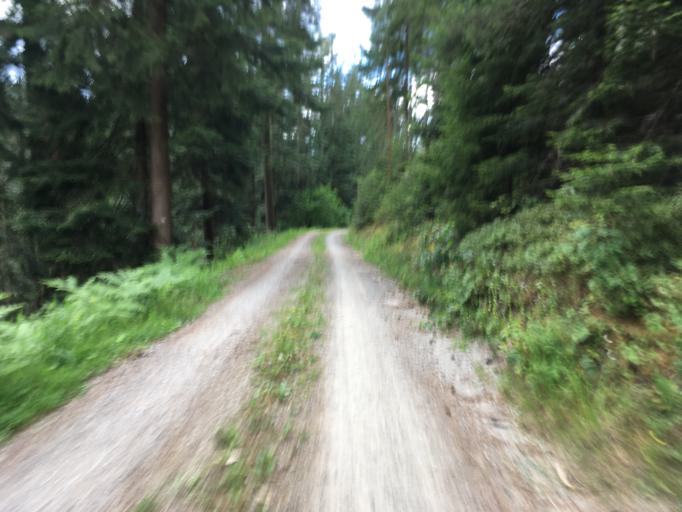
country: DE
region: Baden-Wuerttemberg
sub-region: Karlsruhe Region
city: Alpirsbach
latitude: 48.3480
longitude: 8.4263
